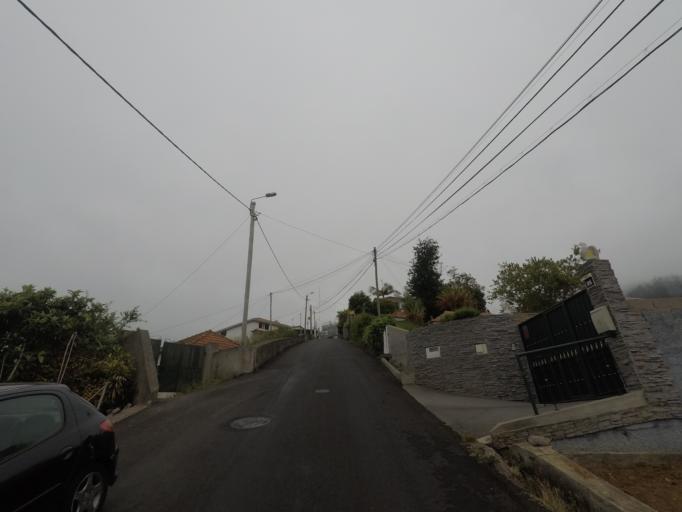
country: PT
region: Madeira
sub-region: Camara de Lobos
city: Curral das Freiras
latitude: 32.6810
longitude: -16.9467
